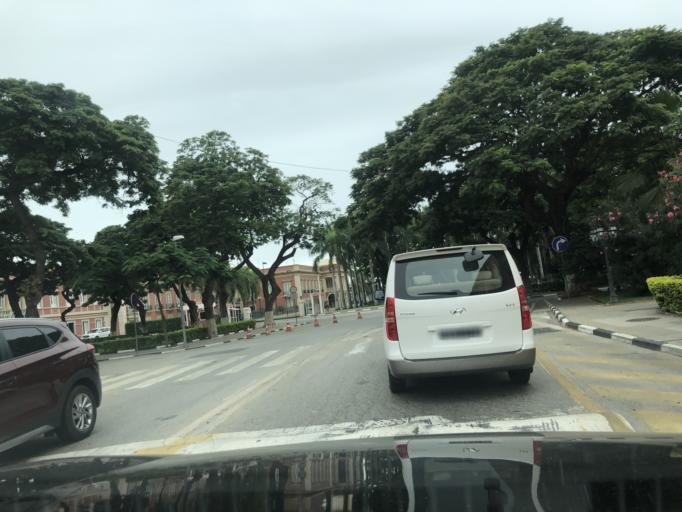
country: AO
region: Luanda
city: Luanda
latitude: -8.8174
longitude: 13.2250
